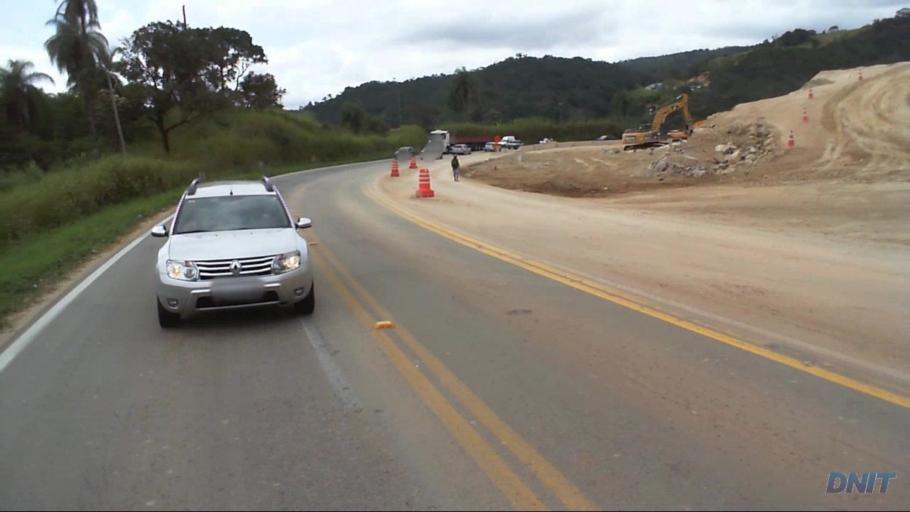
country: BR
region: Minas Gerais
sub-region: Caete
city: Caete
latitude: -19.7838
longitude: -43.6679
